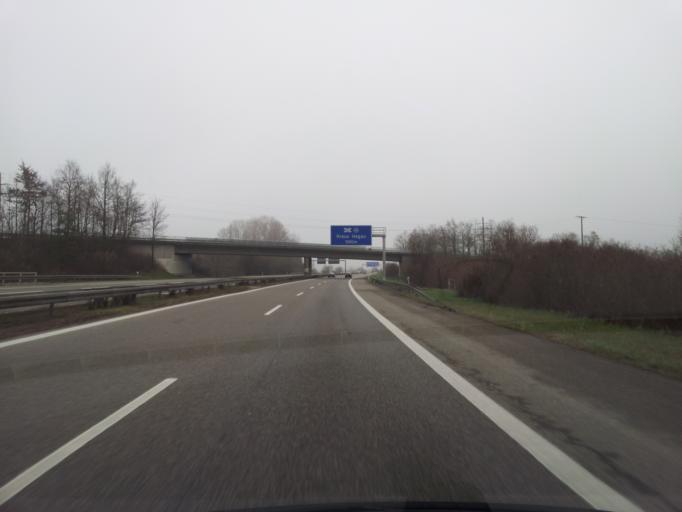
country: DE
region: Baden-Wuerttemberg
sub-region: Freiburg Region
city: Muhlhausen-Ehingen
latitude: 47.7977
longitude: 8.8381
